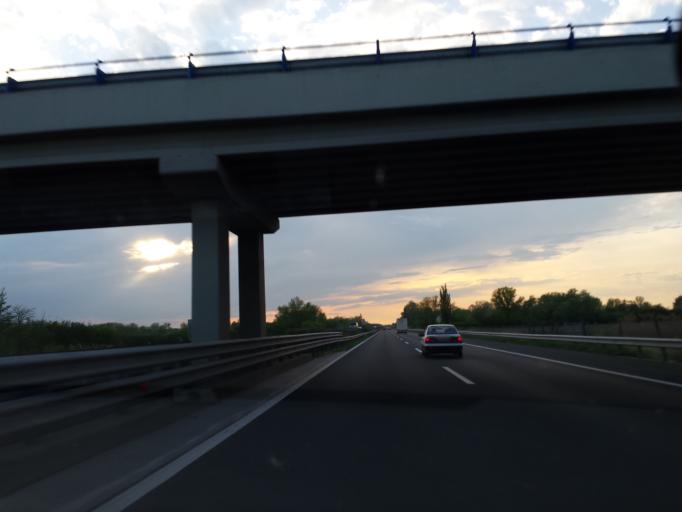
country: HU
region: Gyor-Moson-Sopron
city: Kimle
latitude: 47.7814
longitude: 17.3482
